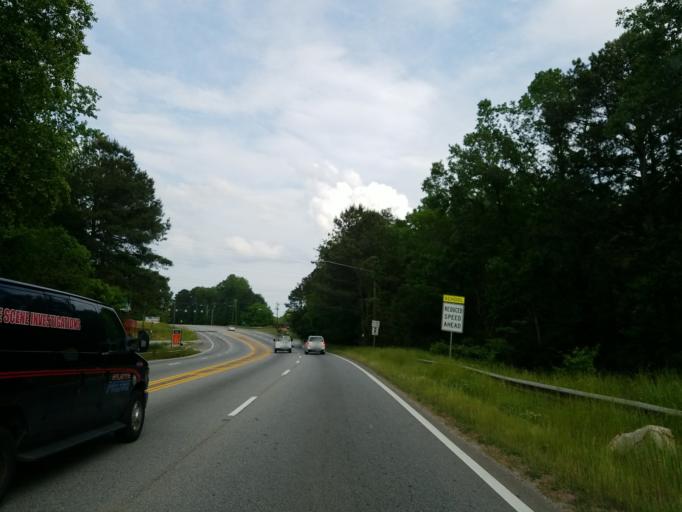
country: US
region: Georgia
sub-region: Cobb County
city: Mableton
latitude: 33.7950
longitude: -84.5069
